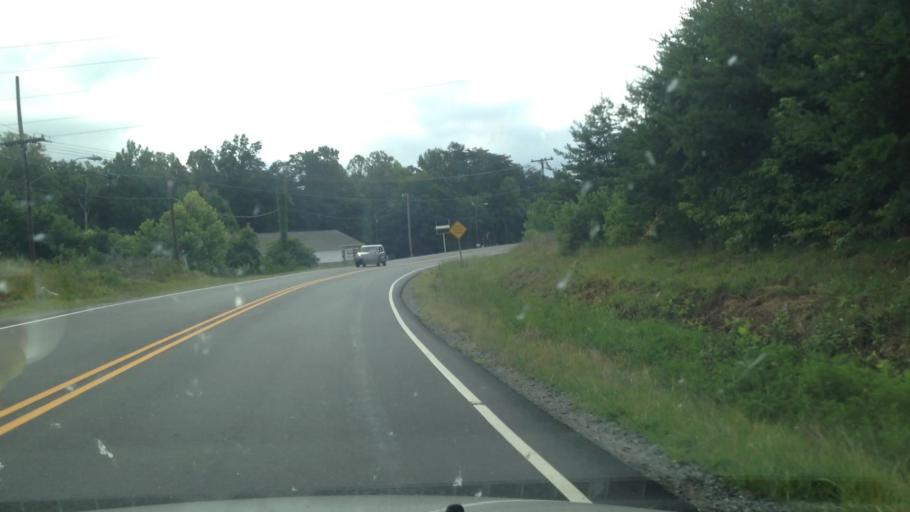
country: US
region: North Carolina
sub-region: Rockingham County
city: Madison
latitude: 36.3844
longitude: -79.9515
